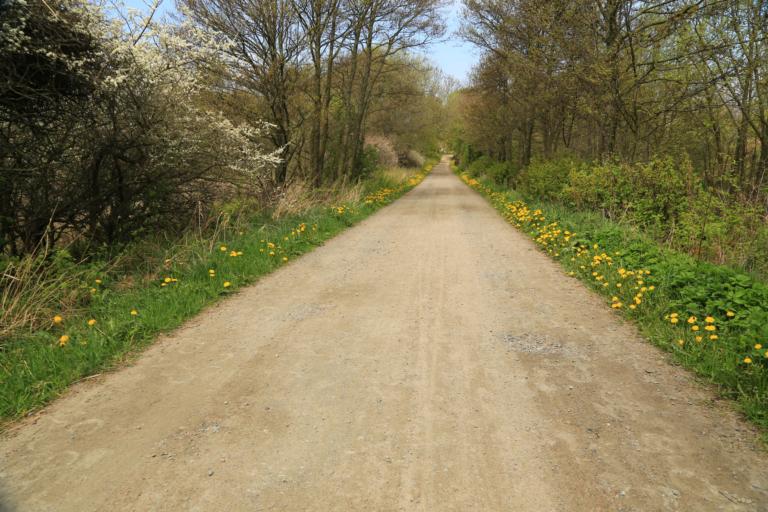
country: SE
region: Halland
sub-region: Varbergs Kommun
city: Varberg
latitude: 57.1320
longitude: 12.2927
